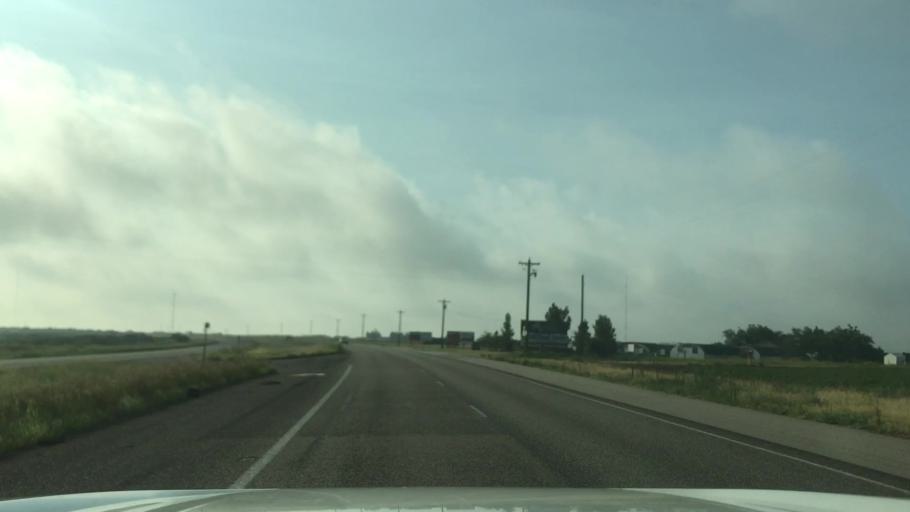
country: US
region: Texas
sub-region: Garza County
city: Post
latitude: 33.2182
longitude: -101.4346
